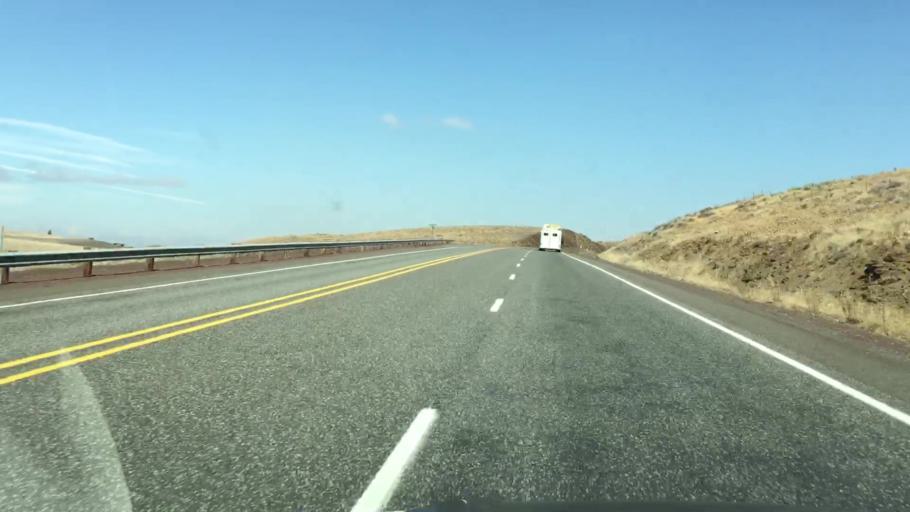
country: US
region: Oregon
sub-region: Wasco County
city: The Dalles
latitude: 45.3184
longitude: -121.1487
